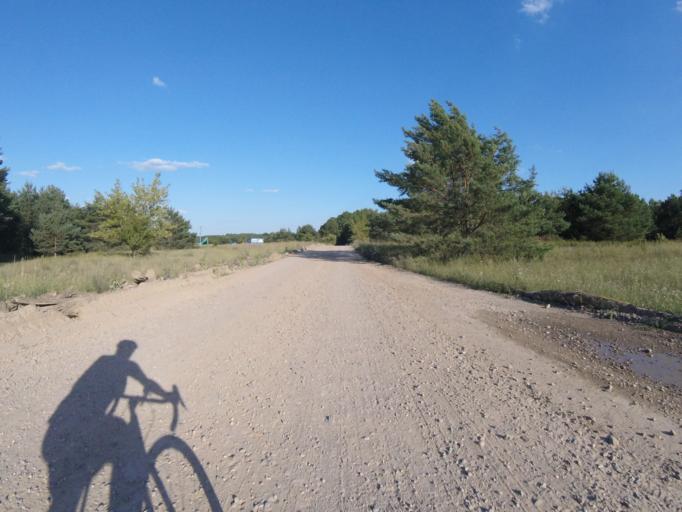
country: DE
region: Brandenburg
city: Zossen
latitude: 52.1979
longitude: 13.5069
